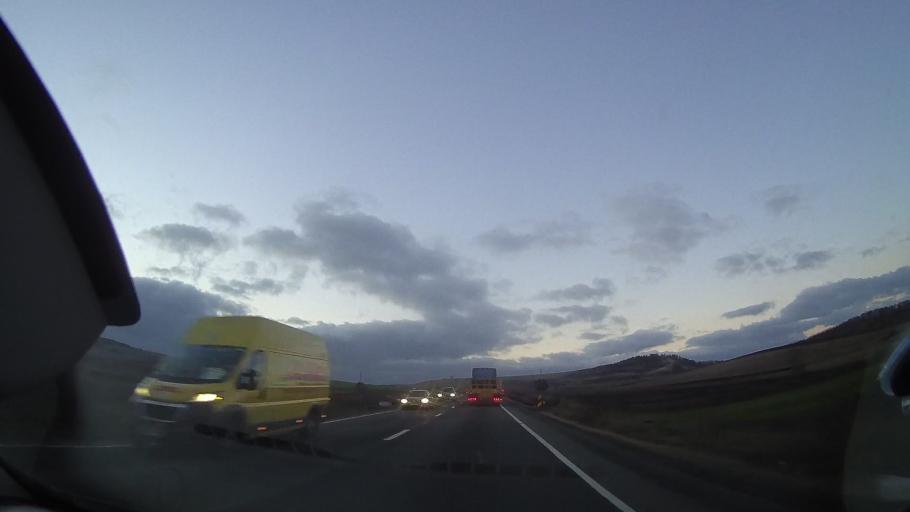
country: RO
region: Cluj
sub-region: Comuna Izvoru Crisului
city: Izvoru Crisului
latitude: 46.8180
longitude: 23.1743
